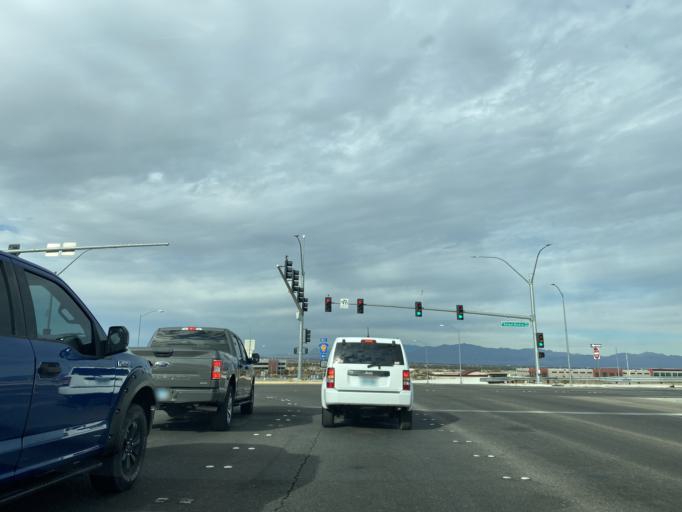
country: US
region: Nevada
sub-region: Clark County
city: Spring Valley
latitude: 36.0667
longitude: -115.2605
